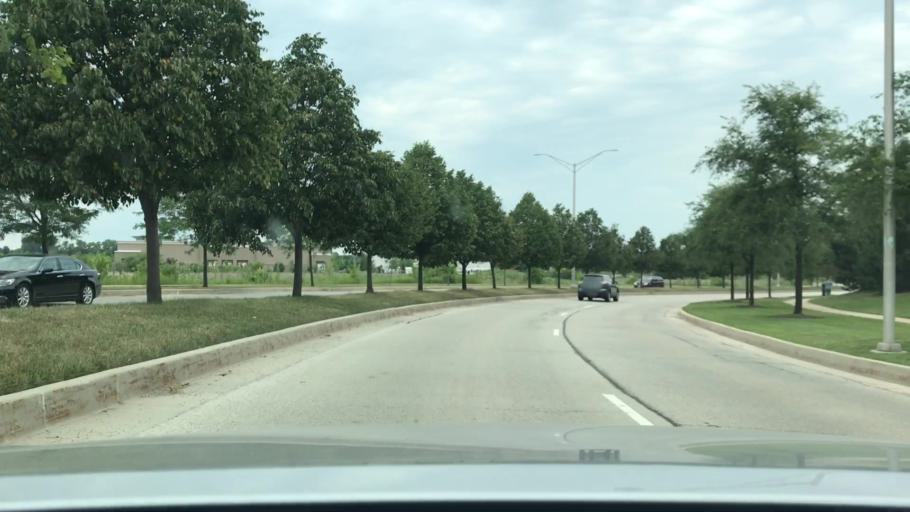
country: US
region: Illinois
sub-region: DuPage County
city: Woodridge
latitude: 41.7174
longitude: -88.0375
